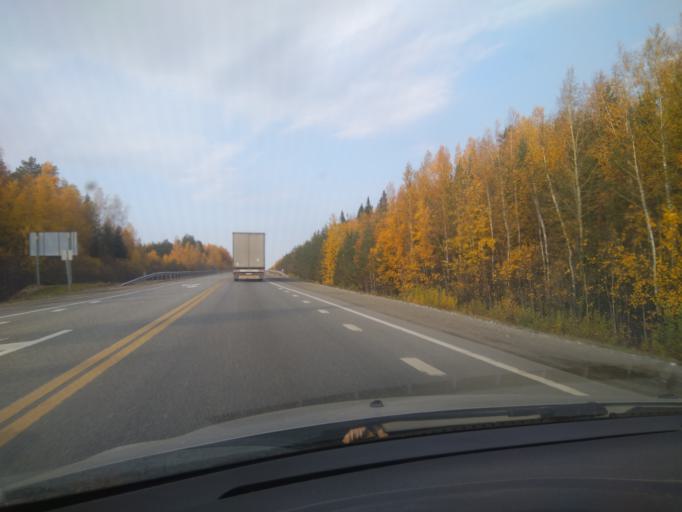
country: RU
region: Sverdlovsk
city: Revda
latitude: 56.8266
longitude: 59.9196
